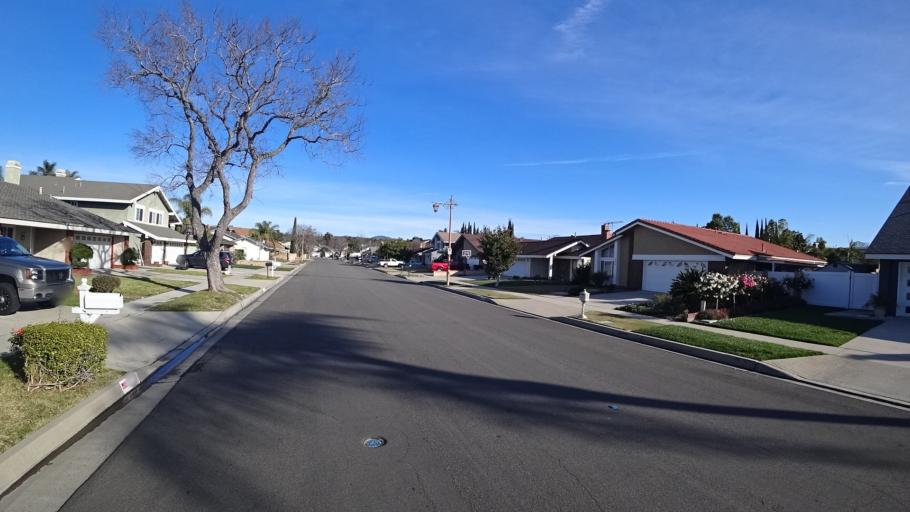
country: US
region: California
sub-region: Orange County
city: Yorba Linda
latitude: 33.8559
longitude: -117.7799
